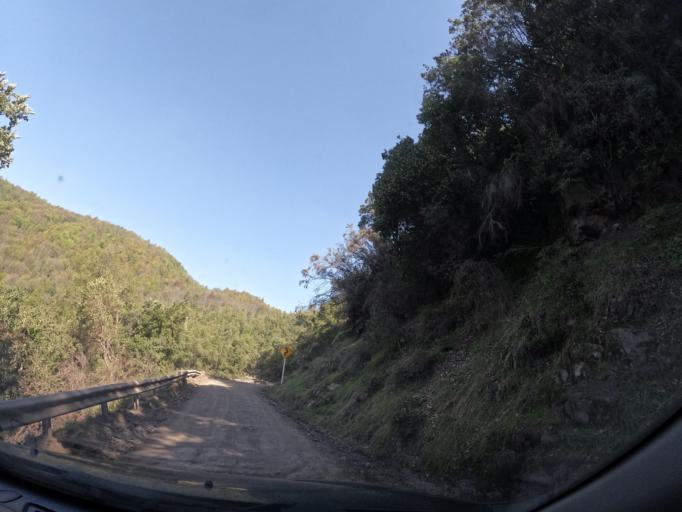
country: CL
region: Maule
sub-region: Provincia de Linares
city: Longavi
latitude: -36.2413
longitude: -71.4410
